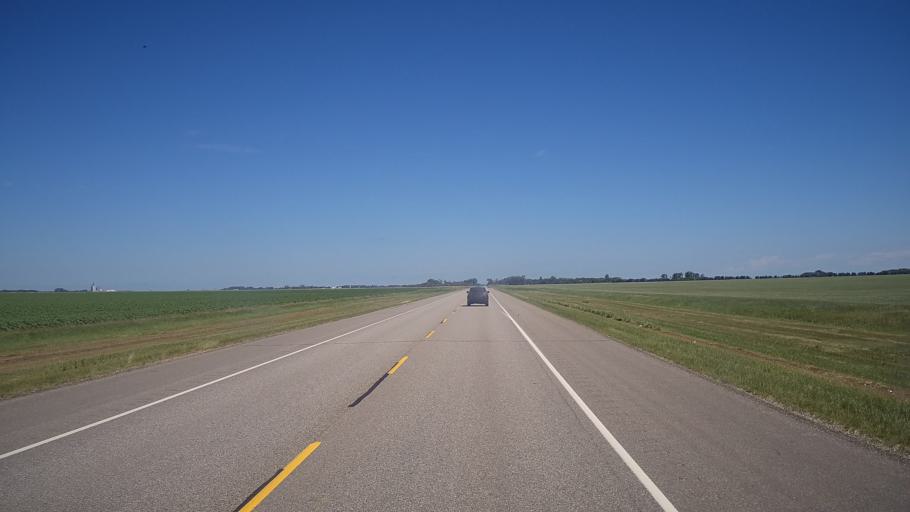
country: CA
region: Manitoba
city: Portage la Prairie
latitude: 50.0373
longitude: -98.4689
